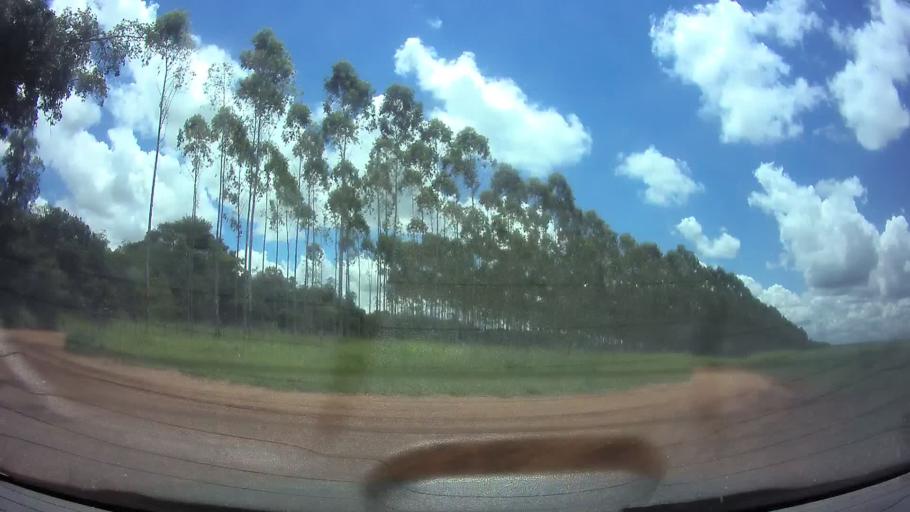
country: PY
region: Paraguari
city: La Colmena
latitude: -25.9679
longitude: -56.7343
